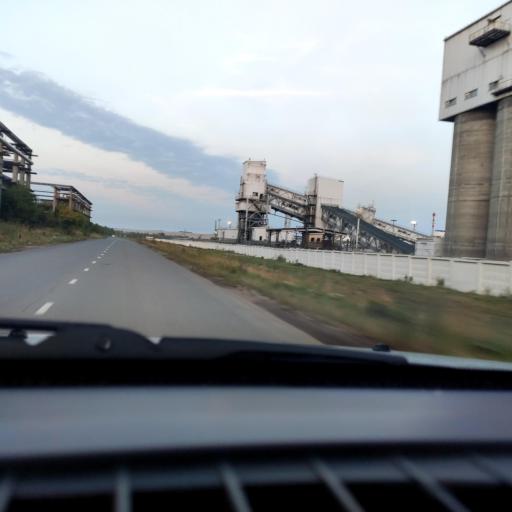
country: RU
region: Perm
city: Gamovo
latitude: 57.9071
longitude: 56.1395
